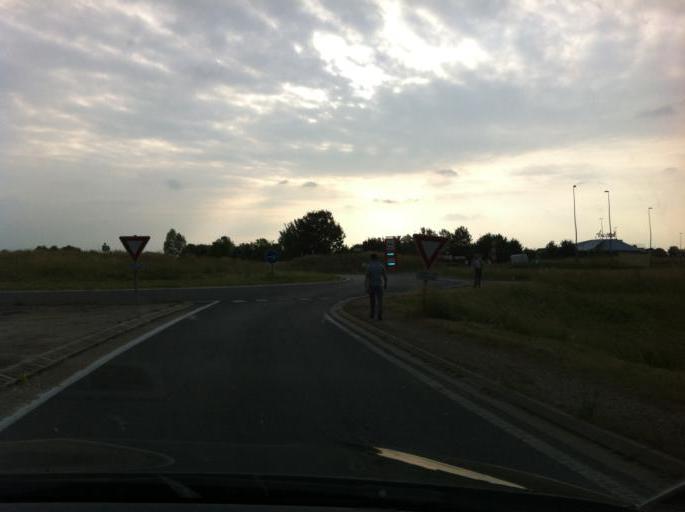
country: FR
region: Ile-de-France
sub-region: Departement de Seine-et-Marne
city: Moissy-Cramayel
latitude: 48.6138
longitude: 2.6304
